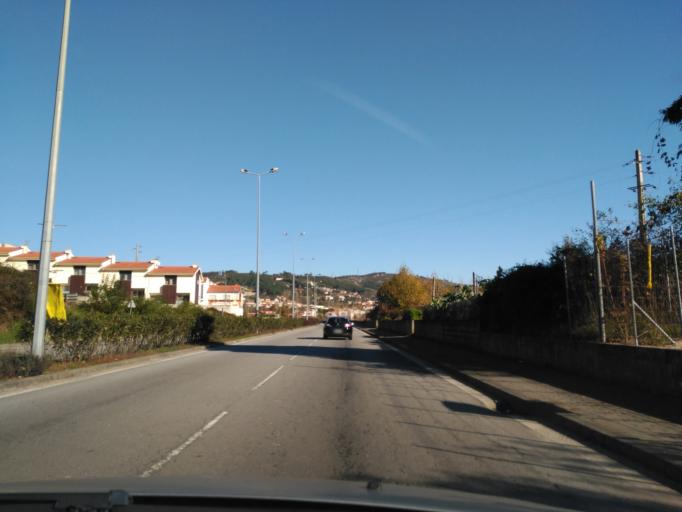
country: PT
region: Braga
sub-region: Braga
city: Adaufe
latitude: 41.5668
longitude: -8.3712
